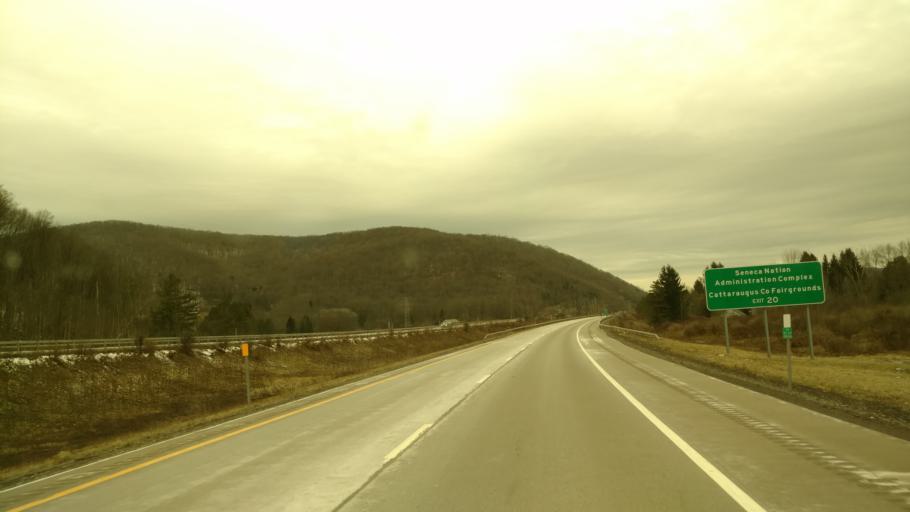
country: US
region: New York
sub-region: Cattaraugus County
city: Salamanca
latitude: 42.1494
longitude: -78.7232
